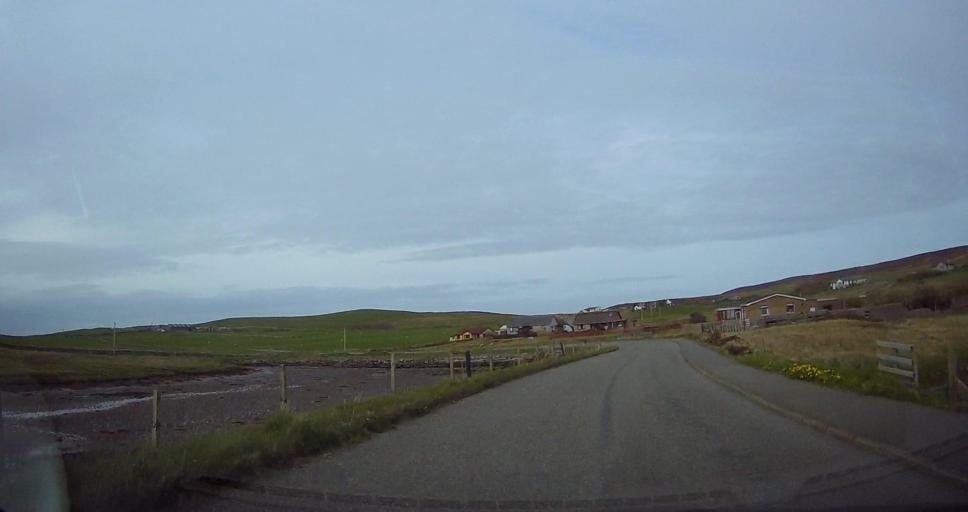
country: GB
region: Scotland
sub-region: Shetland Islands
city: Shetland
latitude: 60.1566
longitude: -1.1152
